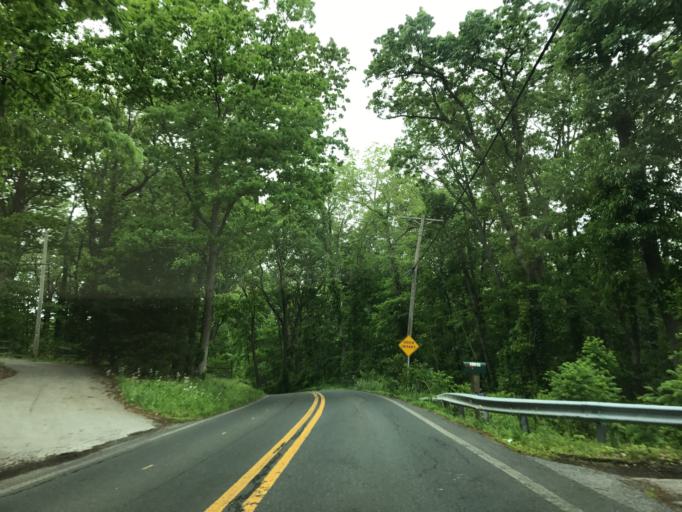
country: US
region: Maryland
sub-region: Carroll County
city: Hampstead
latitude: 39.6007
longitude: -76.8673
